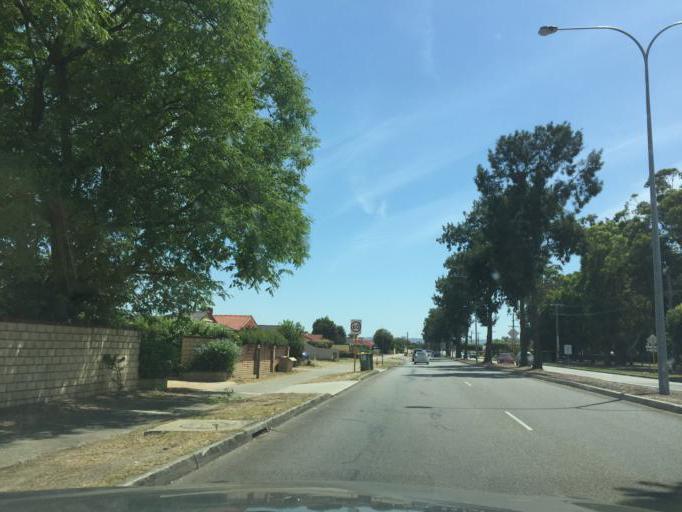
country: AU
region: Western Australia
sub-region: Gosnells
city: Thornlie
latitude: -32.0747
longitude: 115.9618
